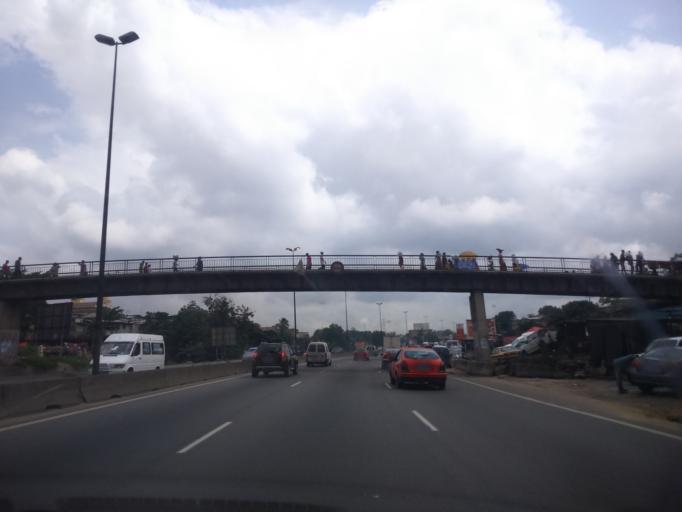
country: CI
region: Lagunes
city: Abidjan
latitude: 5.3613
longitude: -4.0216
